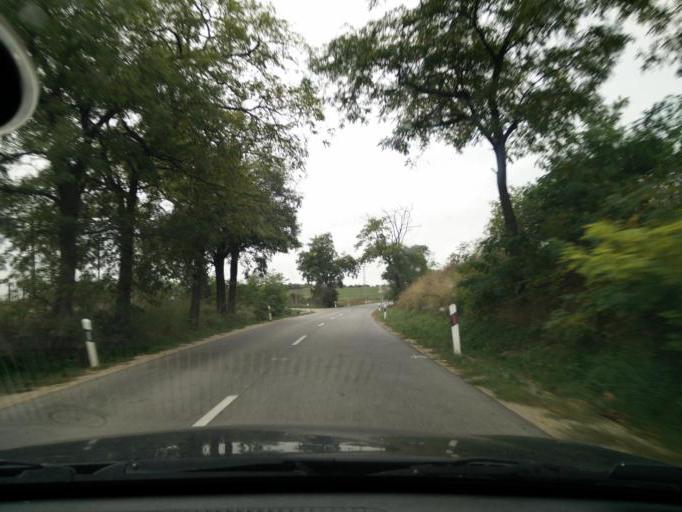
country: HU
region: Komarom-Esztergom
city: Bajna
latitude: 47.6697
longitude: 18.6042
